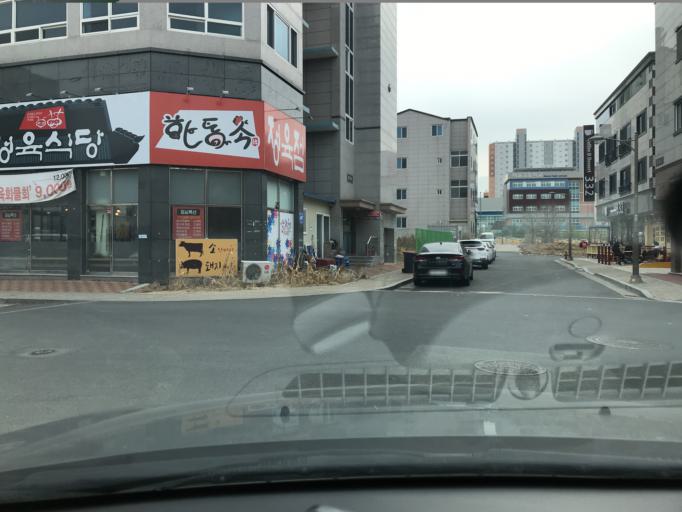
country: KR
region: Daegu
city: Hwawon
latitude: 35.6974
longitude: 128.4542
